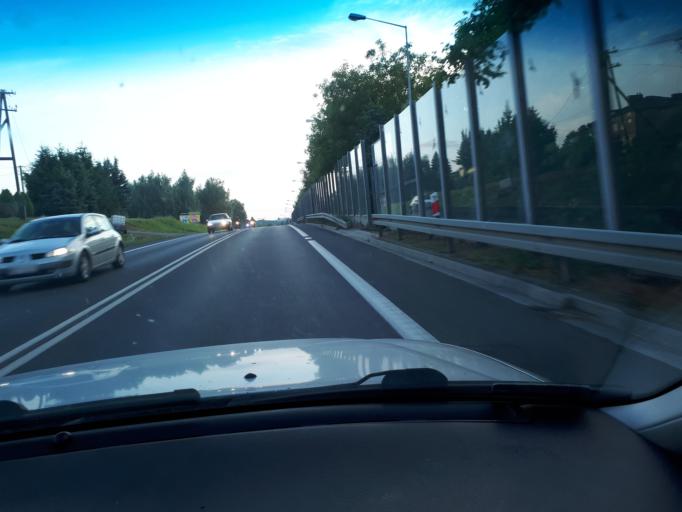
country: PL
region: Subcarpathian Voivodeship
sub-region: Powiat ropczycko-sedziszowski
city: Ropczyce
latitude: 50.0608
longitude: 21.6395
